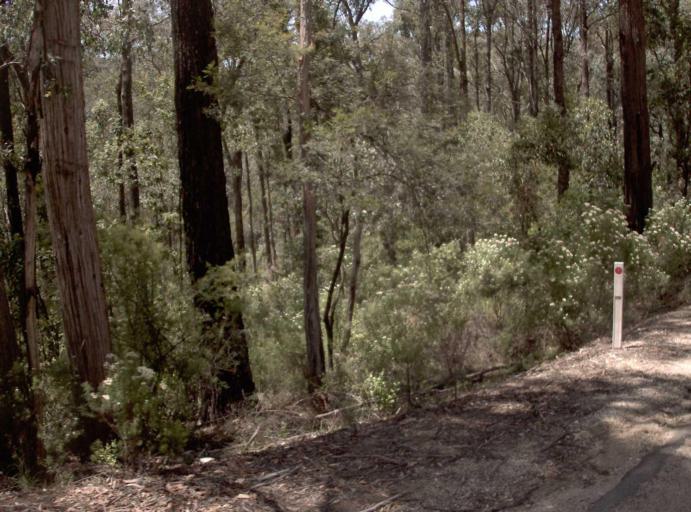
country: AU
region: Victoria
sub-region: East Gippsland
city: Lakes Entrance
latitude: -37.6244
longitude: 147.8833
